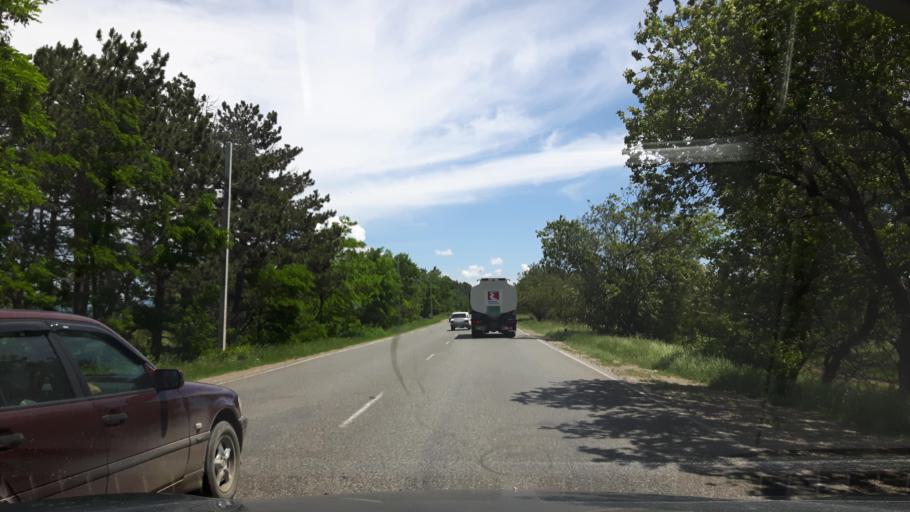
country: GE
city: Didi Lilo
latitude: 41.7002
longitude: 45.1099
